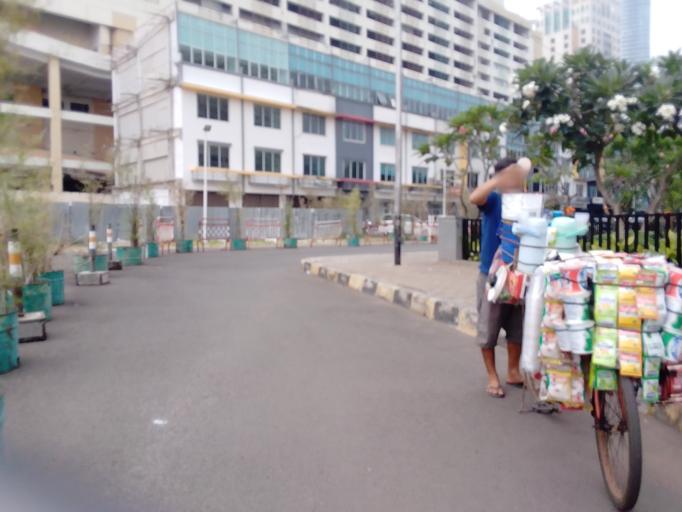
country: ID
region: Jakarta Raya
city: Jakarta
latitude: -6.1959
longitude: 106.8162
